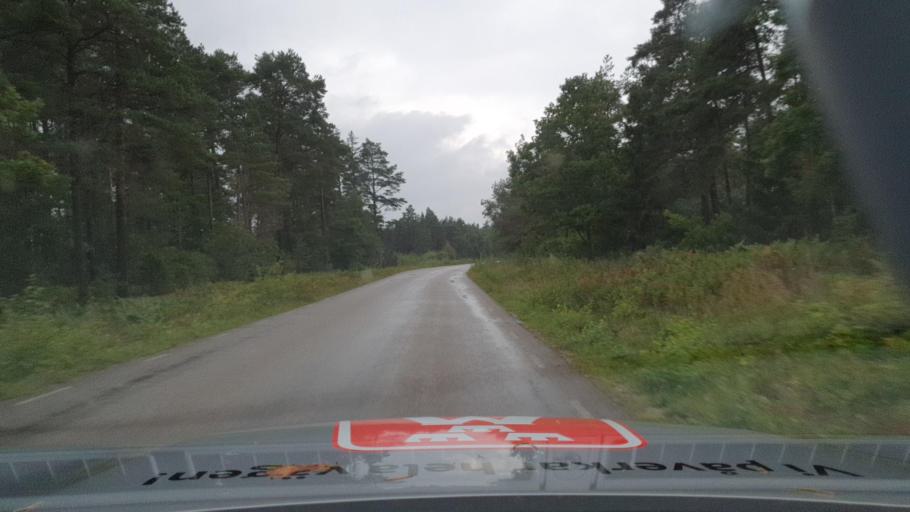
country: SE
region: Gotland
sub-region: Gotland
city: Hemse
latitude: 57.4171
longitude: 18.4401
